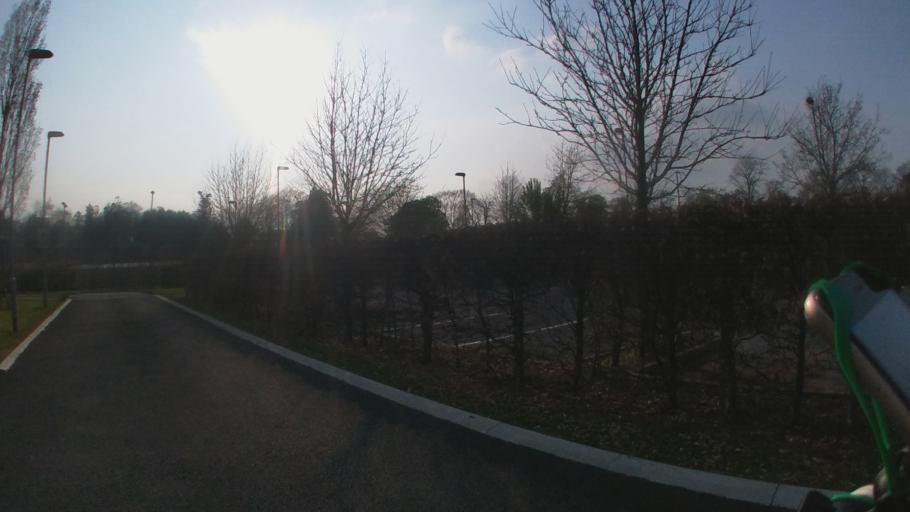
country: IE
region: Leinster
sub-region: Kilkenny
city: Kilkenny
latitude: 52.6384
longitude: -7.2676
